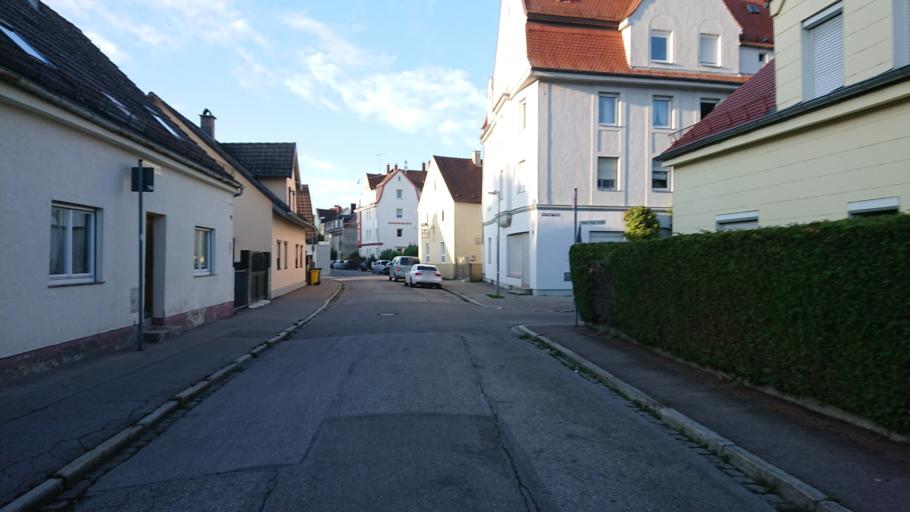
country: DE
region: Bavaria
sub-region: Swabia
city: Stadtbergen
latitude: 48.3637
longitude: 10.8681
